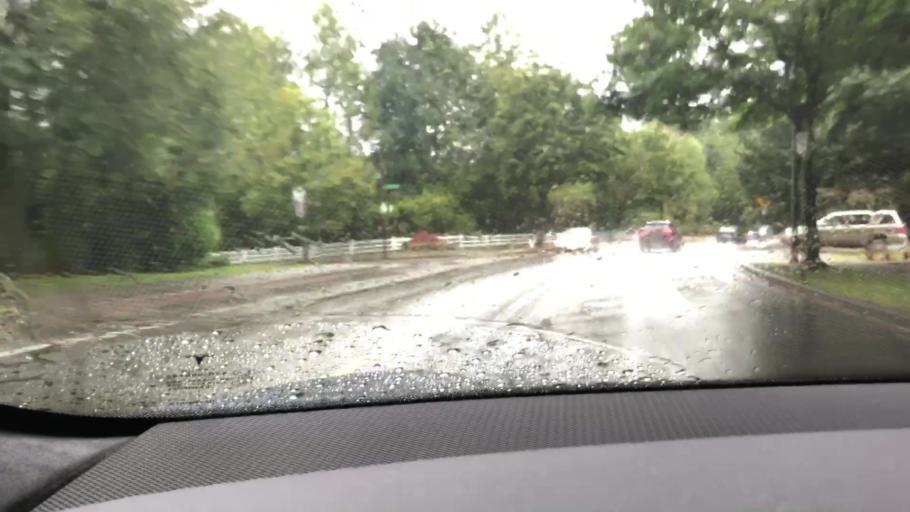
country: CA
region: British Columbia
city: New Westminster
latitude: 49.2381
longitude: -122.9100
